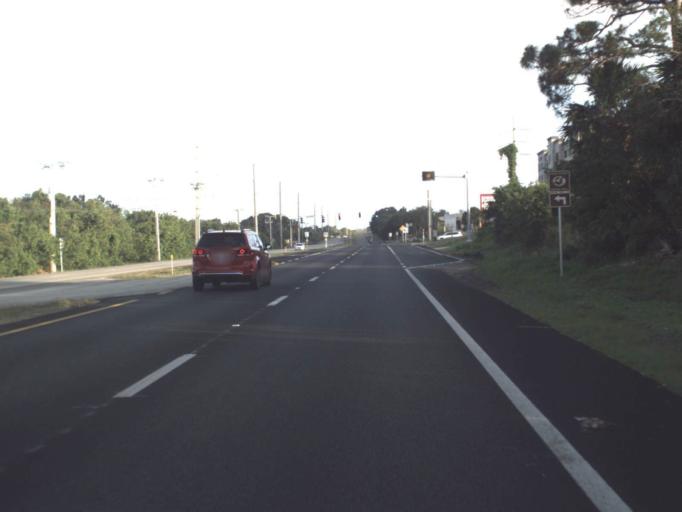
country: US
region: Florida
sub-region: Brevard County
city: South Patrick Shores
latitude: 28.2310
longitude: -80.6738
